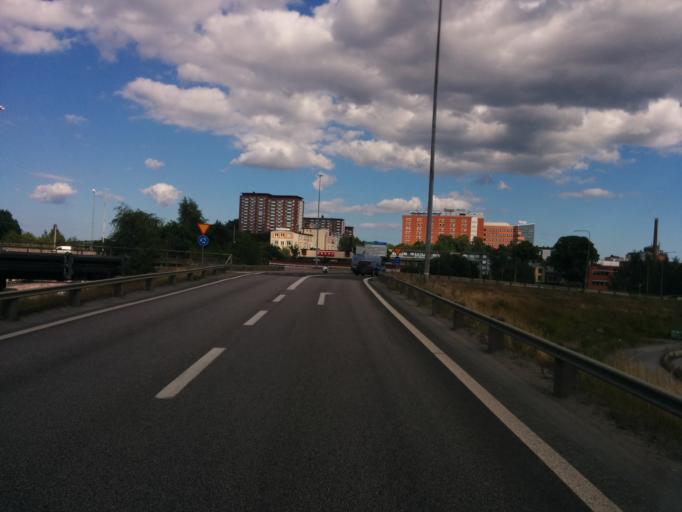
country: SE
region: Stockholm
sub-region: Stockholms Kommun
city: OEstermalm
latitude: 59.3078
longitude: 18.1113
